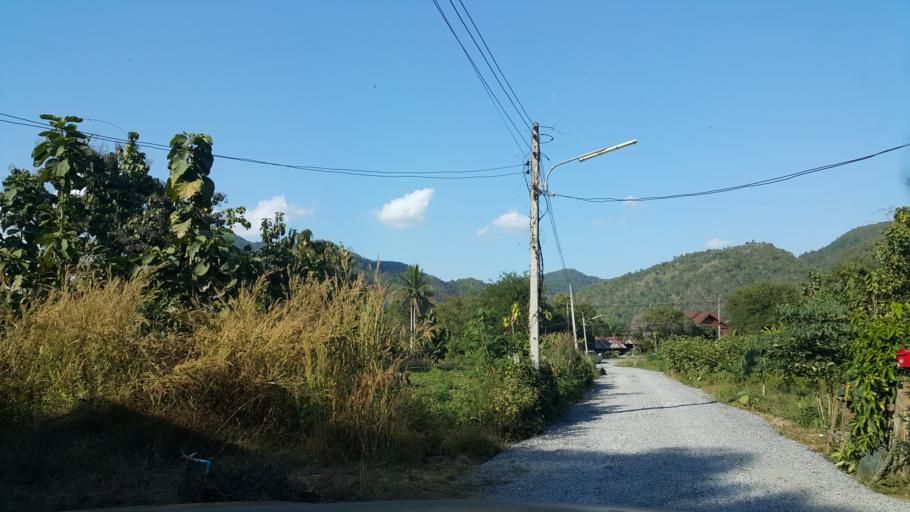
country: TH
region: Sukhothai
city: Thung Saliam
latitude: 17.3416
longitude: 99.4630
